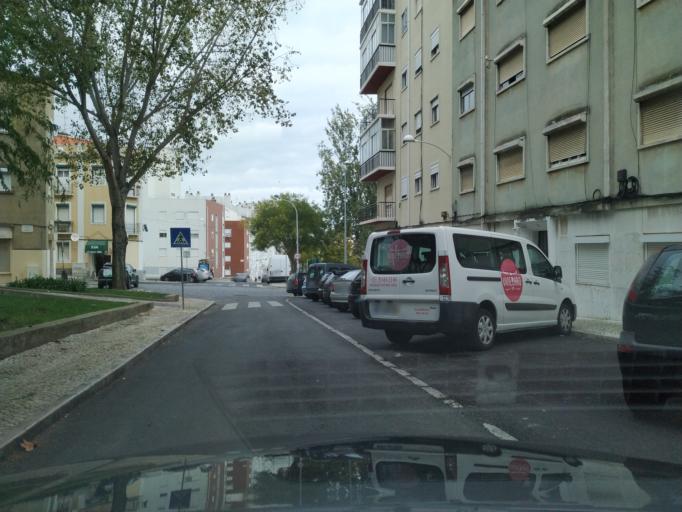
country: PT
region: Lisbon
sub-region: Lisbon
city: Lisbon
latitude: 38.7348
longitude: -9.1219
